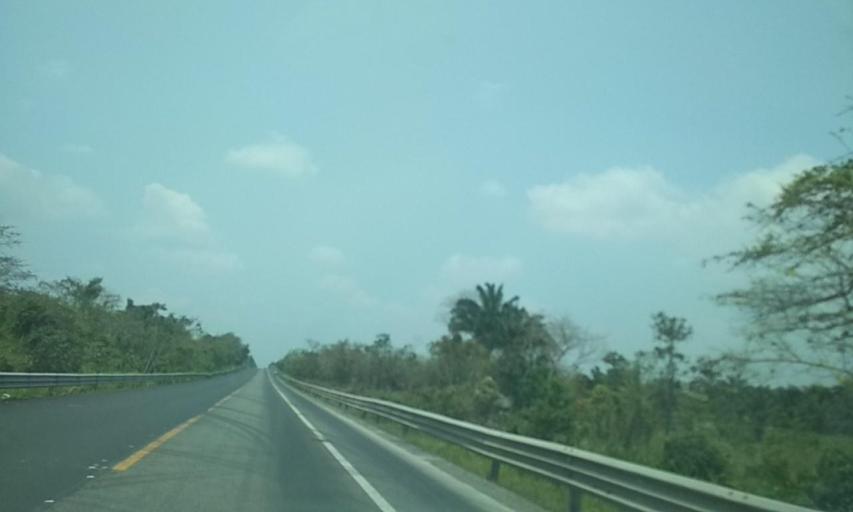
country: MX
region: Tabasco
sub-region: Huimanguillo
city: Francisco Rueda
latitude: 17.7113
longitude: -93.9413
